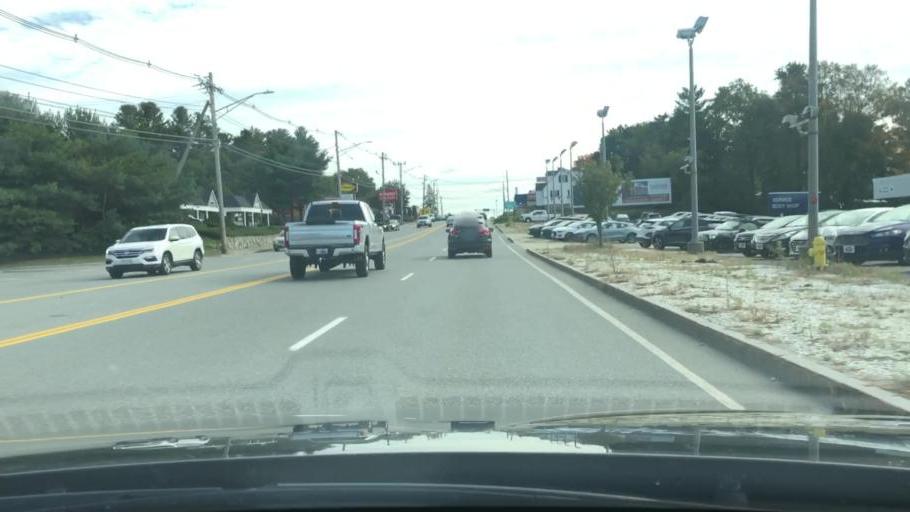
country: US
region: Massachusetts
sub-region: Essex County
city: Methuen
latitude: 42.7462
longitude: -71.2020
